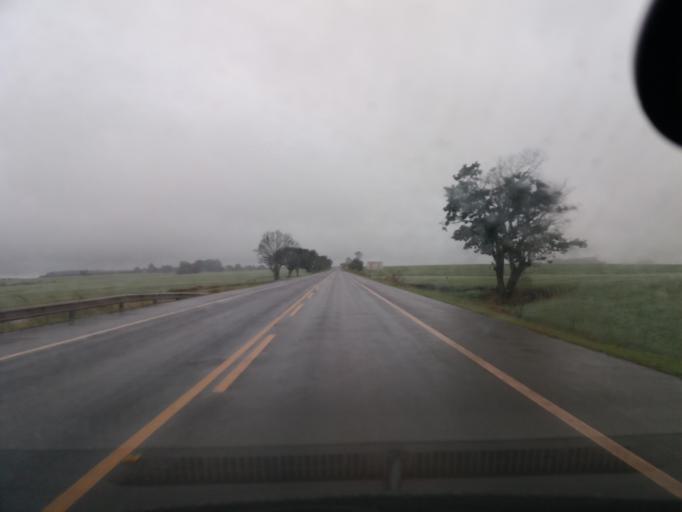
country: BR
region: Parana
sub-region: Campo Mourao
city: Campo Mourao
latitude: -24.3056
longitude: -52.6048
